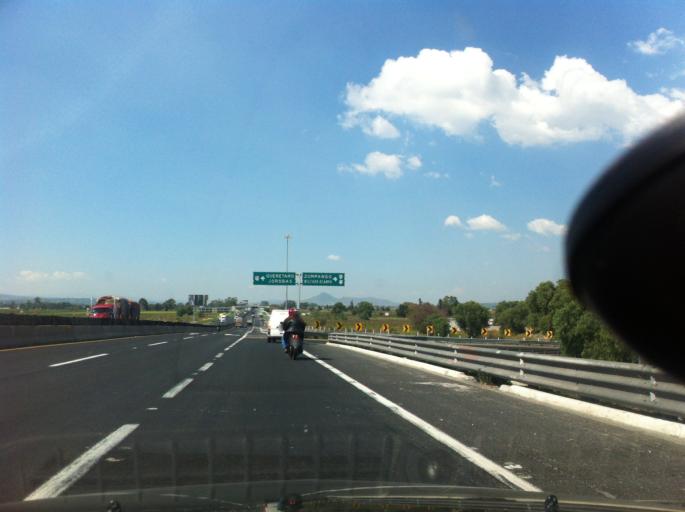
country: MX
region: Mexico
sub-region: Cuautitlan
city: La Providencia
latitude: 19.7525
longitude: -99.1307
